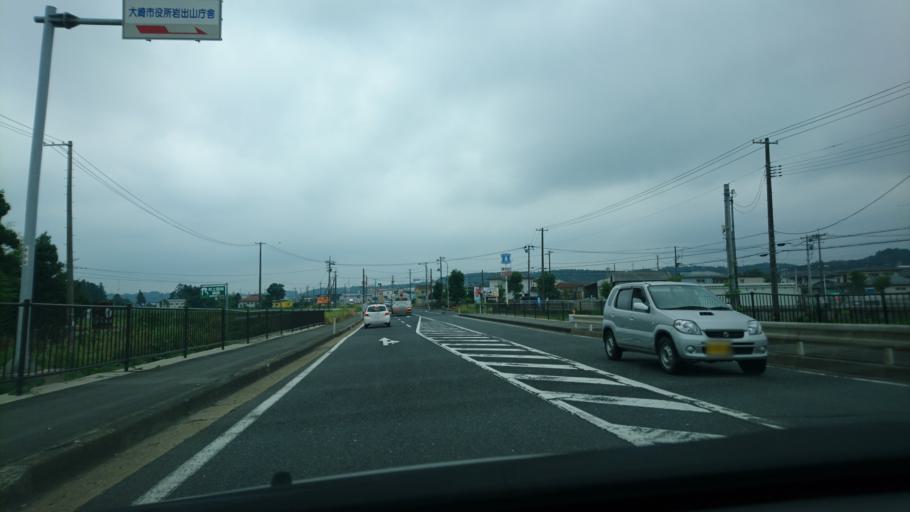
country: JP
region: Miyagi
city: Furukawa
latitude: 38.6506
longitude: 140.8782
